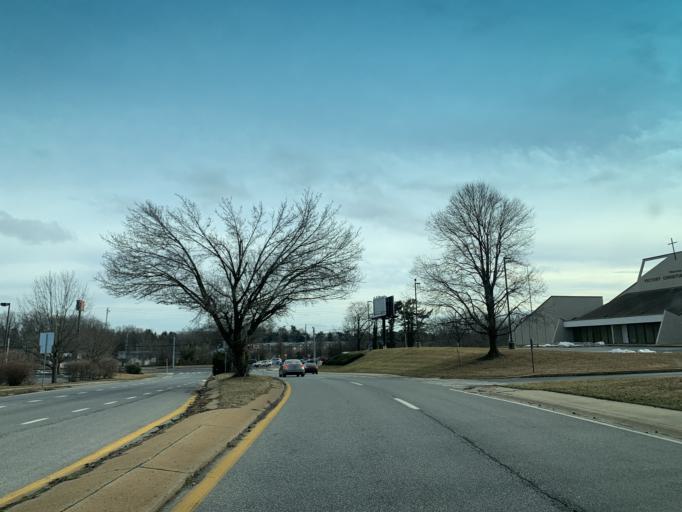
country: US
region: Delaware
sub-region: New Castle County
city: Bear
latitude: 39.6520
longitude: -75.6233
